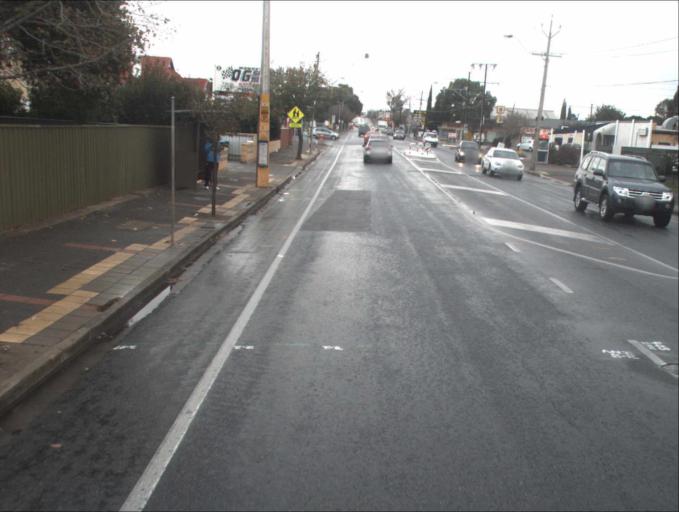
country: AU
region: South Australia
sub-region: Port Adelaide Enfield
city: Klemzig
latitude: -34.8830
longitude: 138.6371
